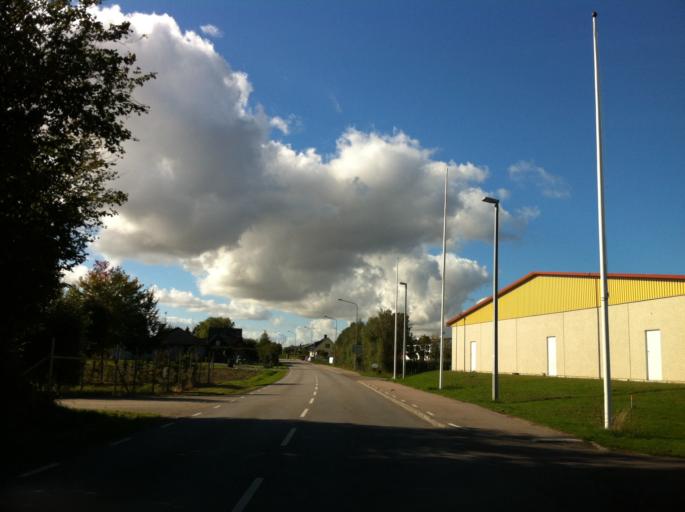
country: SE
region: Skane
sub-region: Eslovs Kommun
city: Eslov
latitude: 55.7510
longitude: 13.3765
